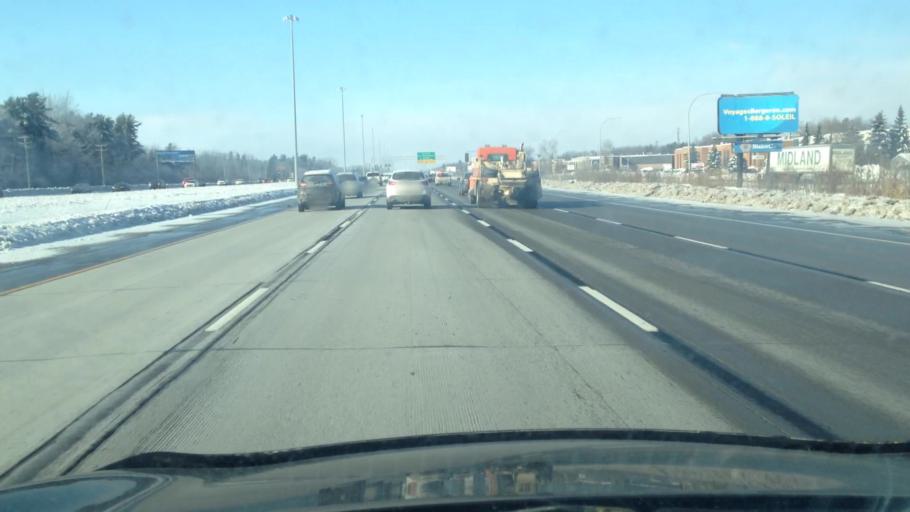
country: CA
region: Quebec
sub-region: Laurentides
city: Blainville
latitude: 45.6651
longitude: -73.8953
